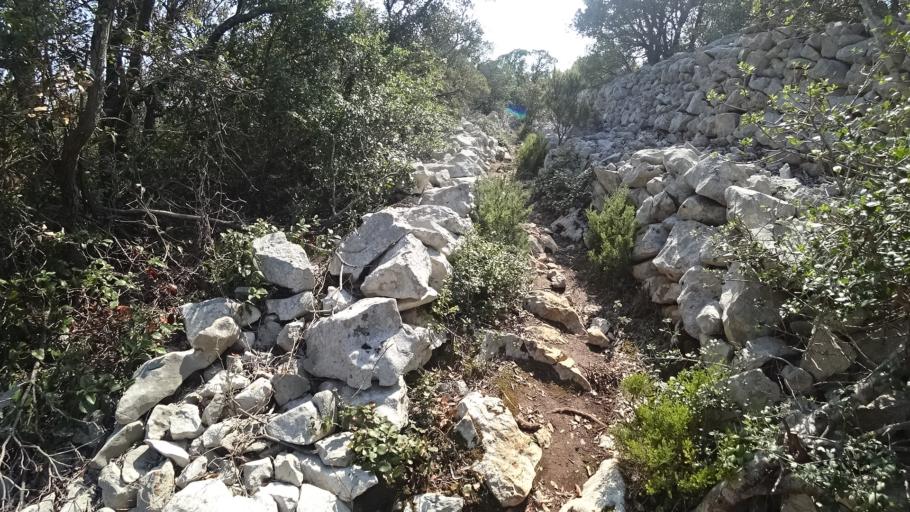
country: HR
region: Primorsko-Goranska
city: Mali Losinj
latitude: 44.4936
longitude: 14.5303
